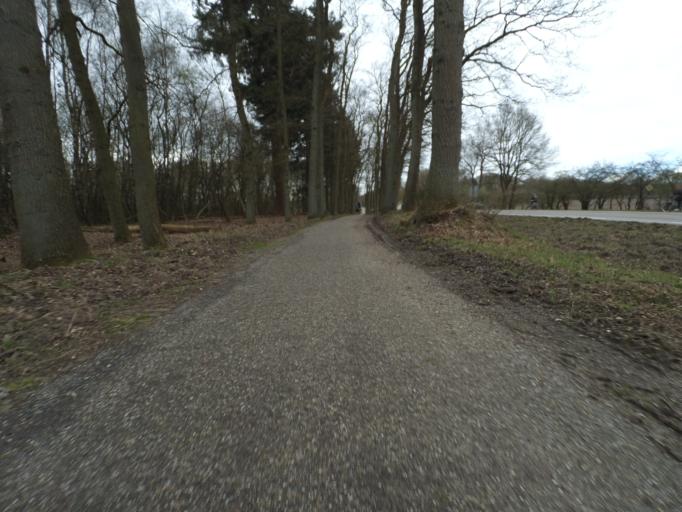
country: NL
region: Gelderland
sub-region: Gemeente Apeldoorn
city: Beekbergen
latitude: 52.1066
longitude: 5.9524
